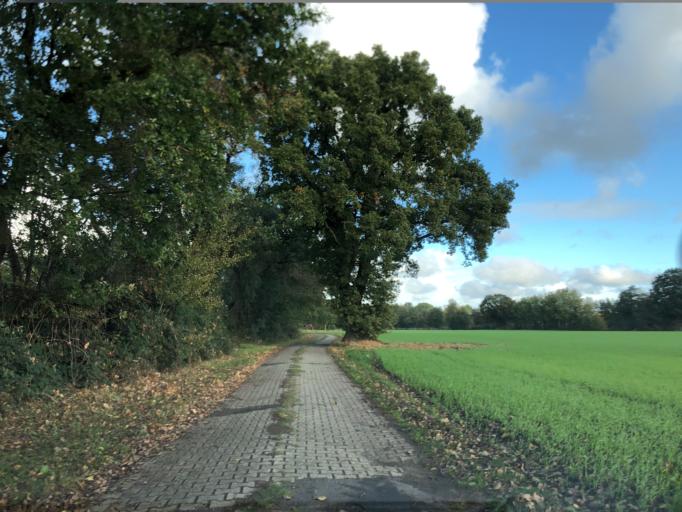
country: DE
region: Lower Saxony
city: Lehe
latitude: 53.0319
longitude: 7.3359
